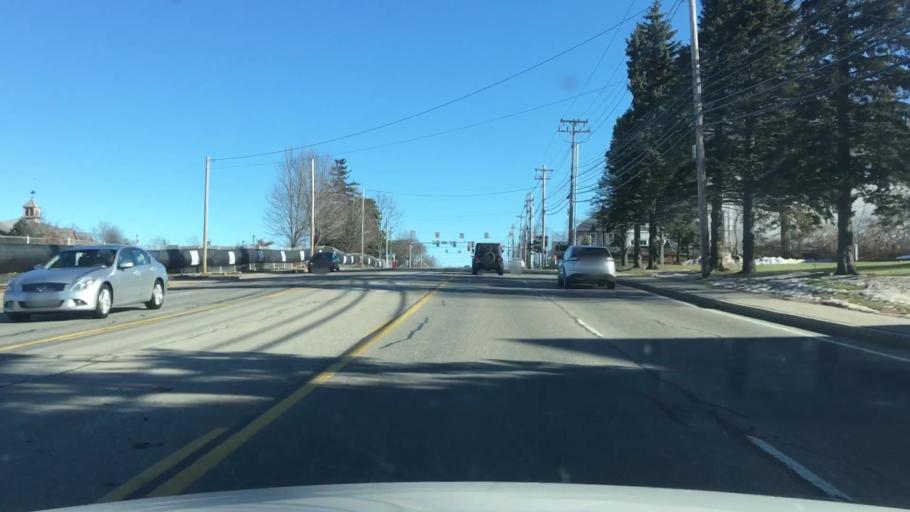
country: US
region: Maine
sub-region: Cumberland County
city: Scarborough
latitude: 43.5890
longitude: -70.3412
